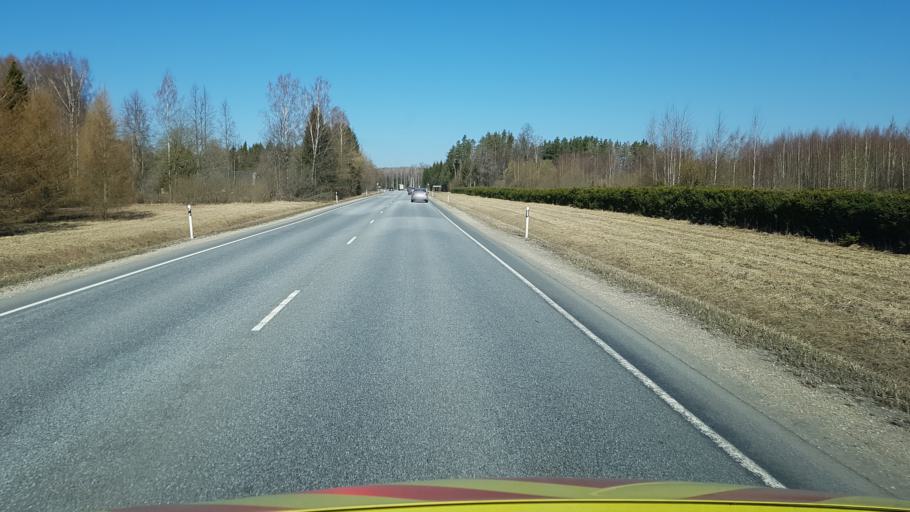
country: EE
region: Jogevamaa
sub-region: Poltsamaa linn
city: Poltsamaa
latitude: 58.6107
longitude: 26.1972
